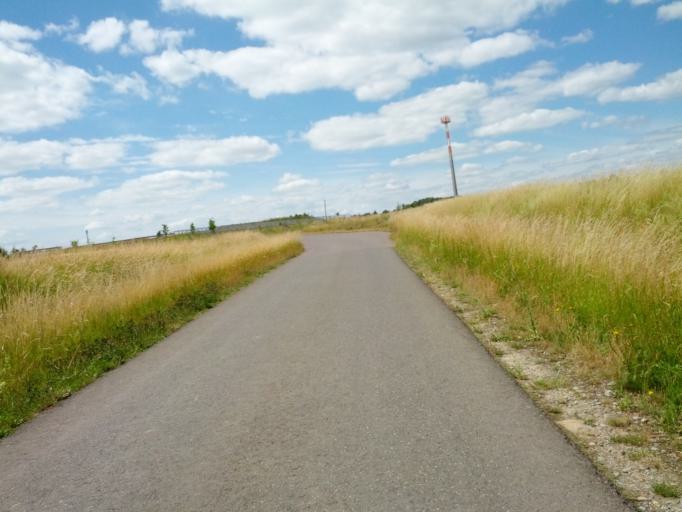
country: DE
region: Thuringia
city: Bischofroda
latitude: 51.0151
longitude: 10.3514
